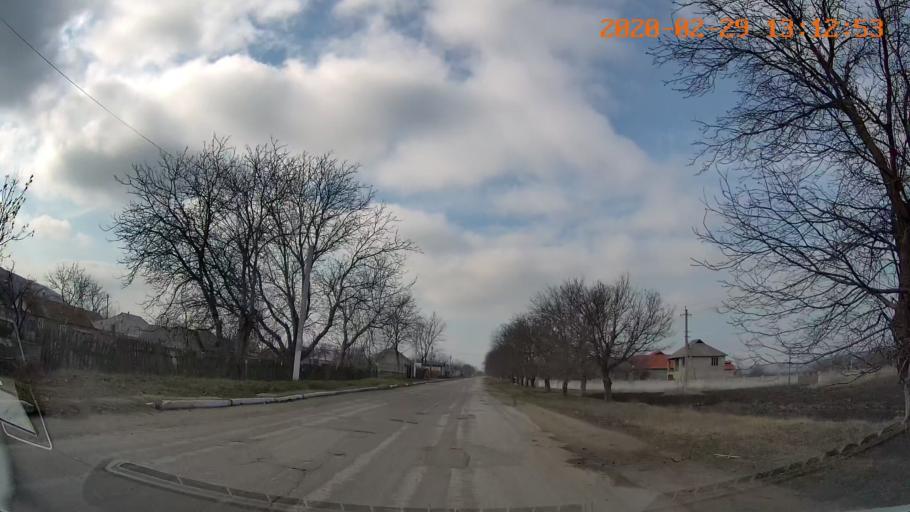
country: MD
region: Telenesti
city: Camenca
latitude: 48.0134
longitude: 28.6907
